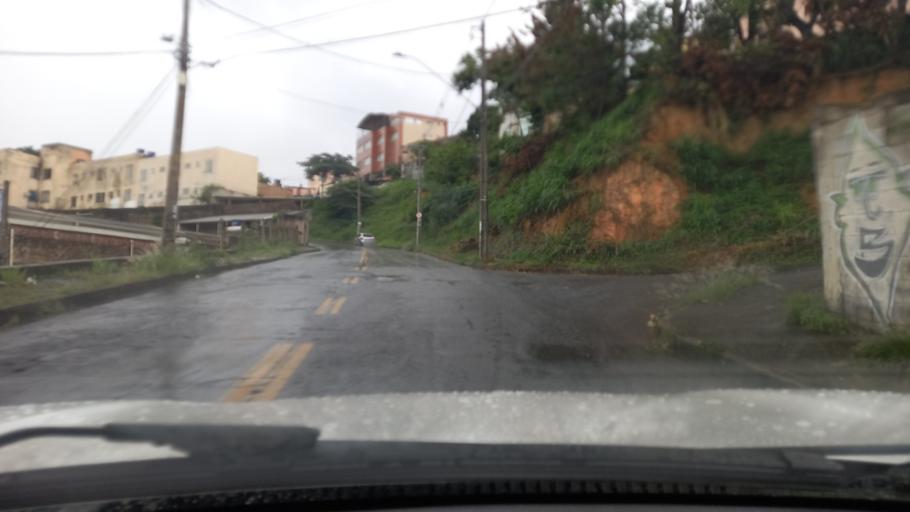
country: BR
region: Minas Gerais
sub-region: Belo Horizonte
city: Belo Horizonte
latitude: -19.8970
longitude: -43.9497
